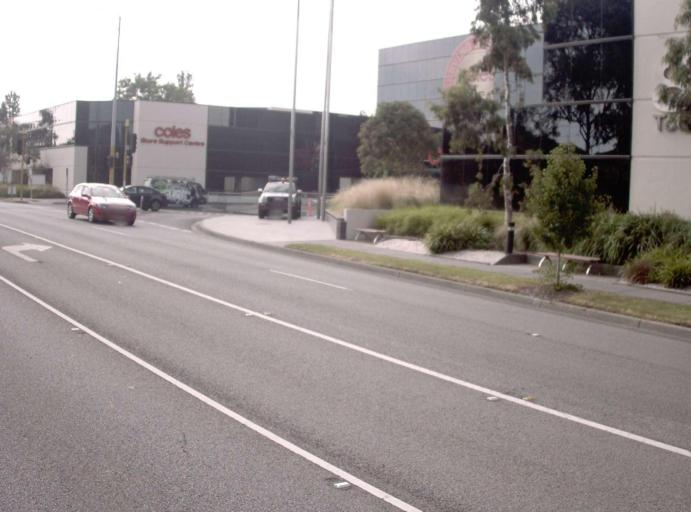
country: AU
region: Victoria
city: Glenferrie
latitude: -37.8452
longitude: 145.0476
